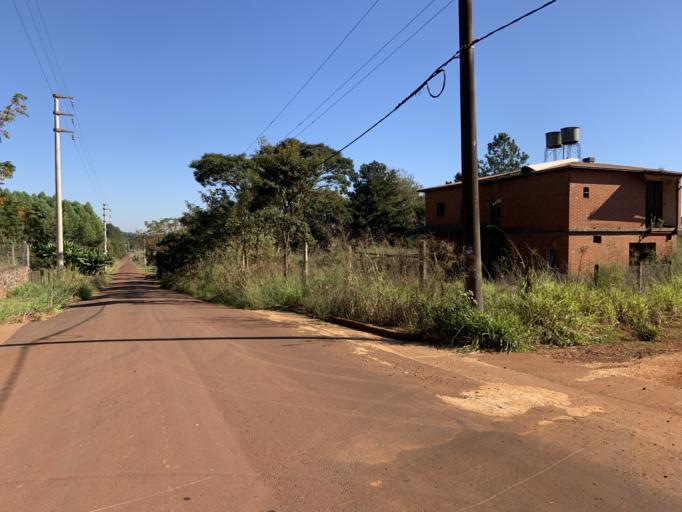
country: AR
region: Misiones
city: Puerto Rico
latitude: -26.8333
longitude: -55.0266
